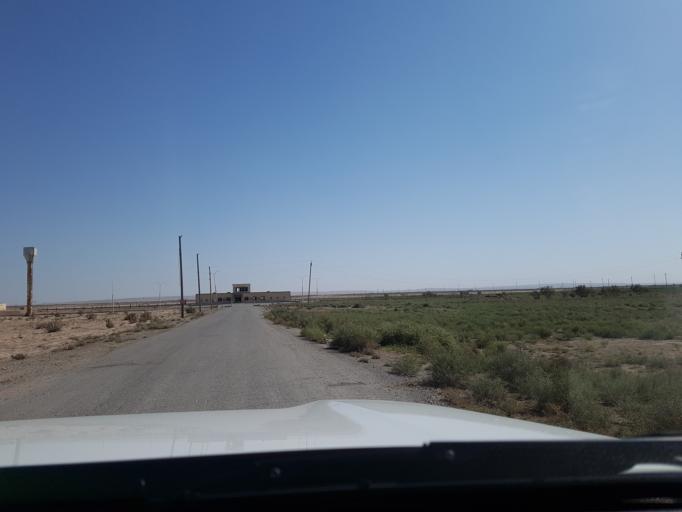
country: IR
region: Razavi Khorasan
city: Sarakhs
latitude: 36.4934
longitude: 61.2544
